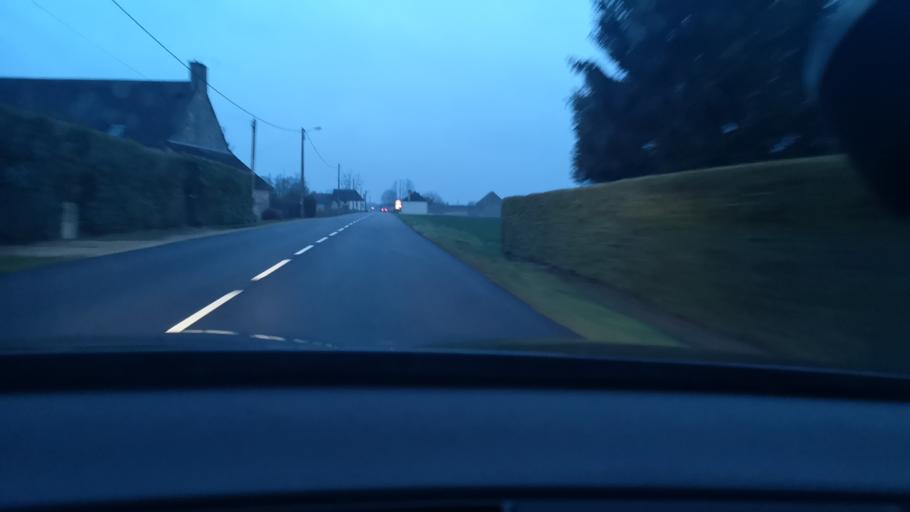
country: FR
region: Bourgogne
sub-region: Departement de Saone-et-Loire
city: Demigny
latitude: 46.9370
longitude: 4.8596
